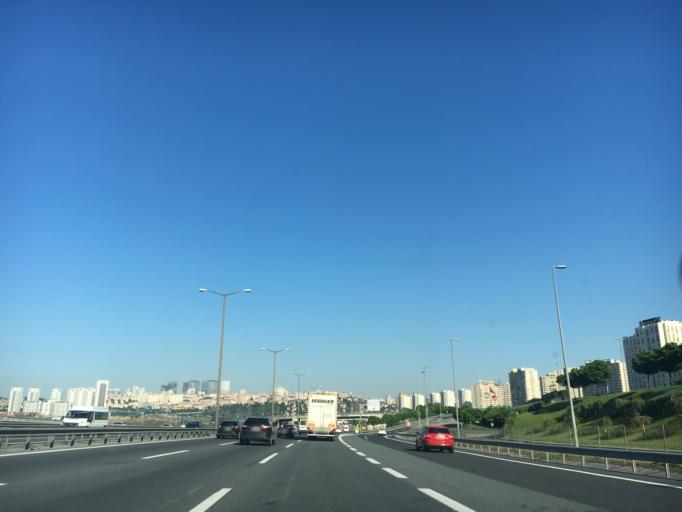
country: TR
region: Istanbul
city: Esenyurt
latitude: 41.0552
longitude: 28.7159
